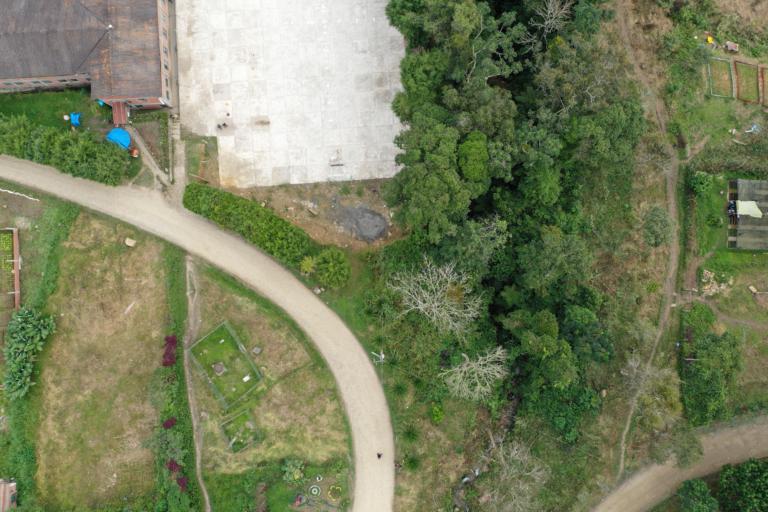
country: BO
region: La Paz
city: Coroico
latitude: -16.2577
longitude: -67.6920
